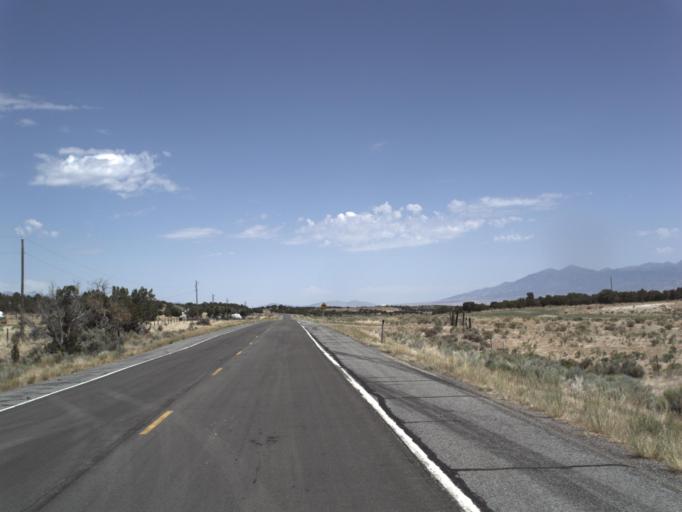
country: US
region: Utah
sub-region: Utah County
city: Eagle Mountain
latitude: 40.0192
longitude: -112.2796
